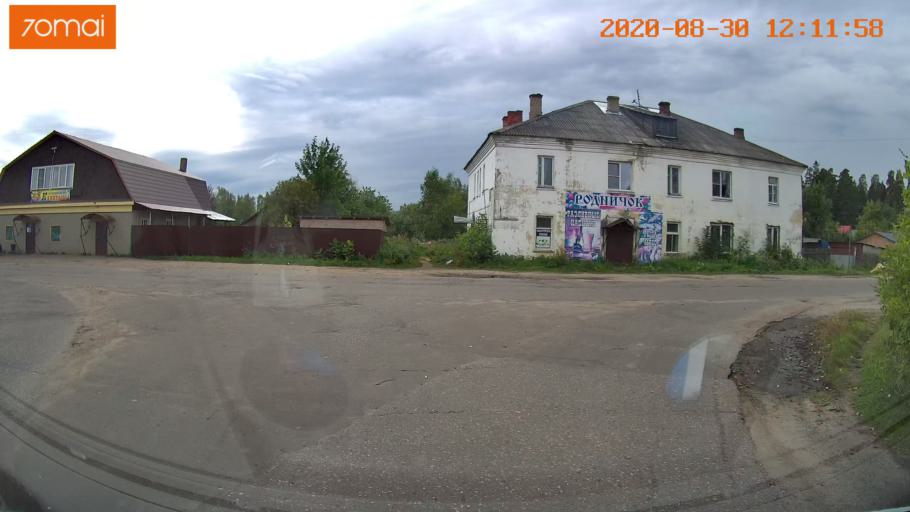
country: RU
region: Ivanovo
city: Yur'yevets
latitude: 57.3111
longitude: 43.0969
